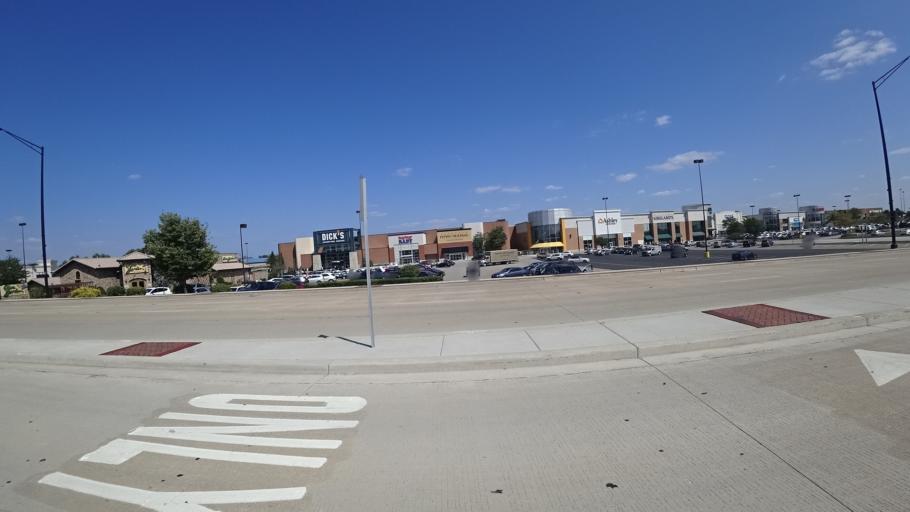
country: US
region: Illinois
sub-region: Cook County
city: Orland Park
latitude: 41.6131
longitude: -87.8534
